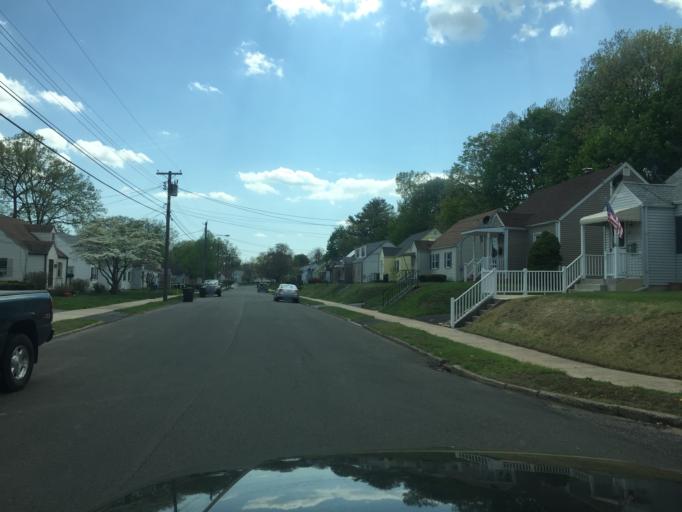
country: US
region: Connecticut
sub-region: Hartford County
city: New Britain
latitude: 41.6926
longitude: -72.7937
